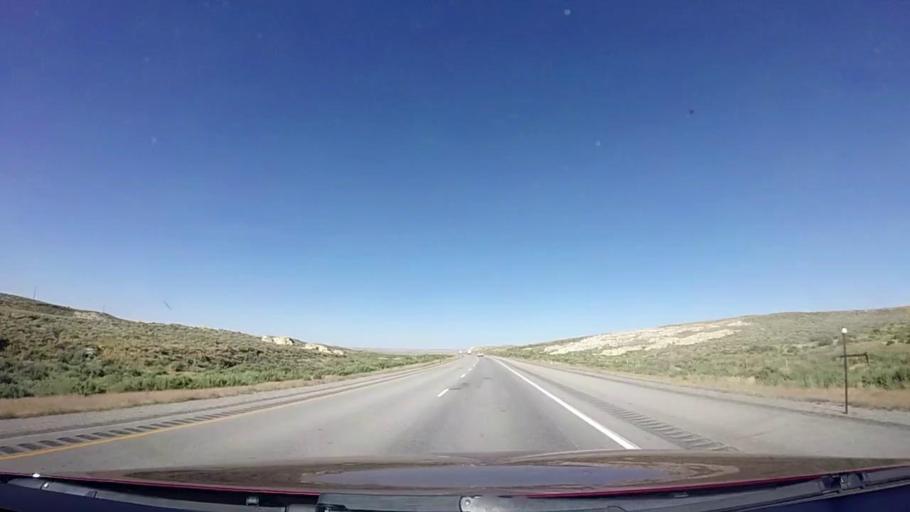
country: US
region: Wyoming
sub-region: Carbon County
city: Rawlins
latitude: 41.7892
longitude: -107.3903
